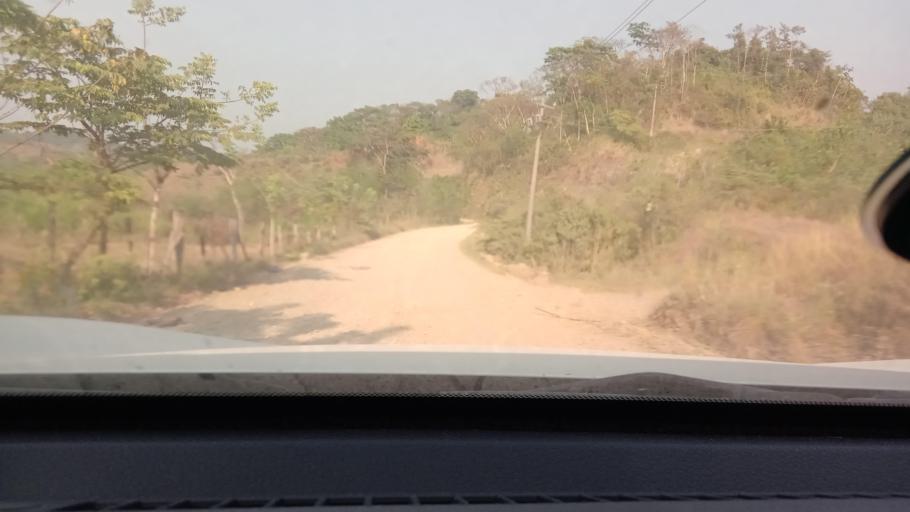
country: MX
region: Tabasco
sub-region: Huimanguillo
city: Francisco Rueda
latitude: 17.6532
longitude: -93.8790
